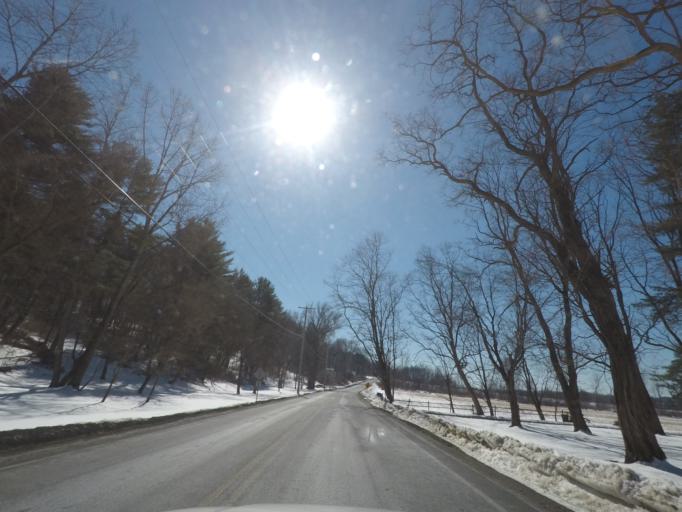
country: US
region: New York
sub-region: Saratoga County
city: Schuylerville
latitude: 43.0993
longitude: -73.5667
